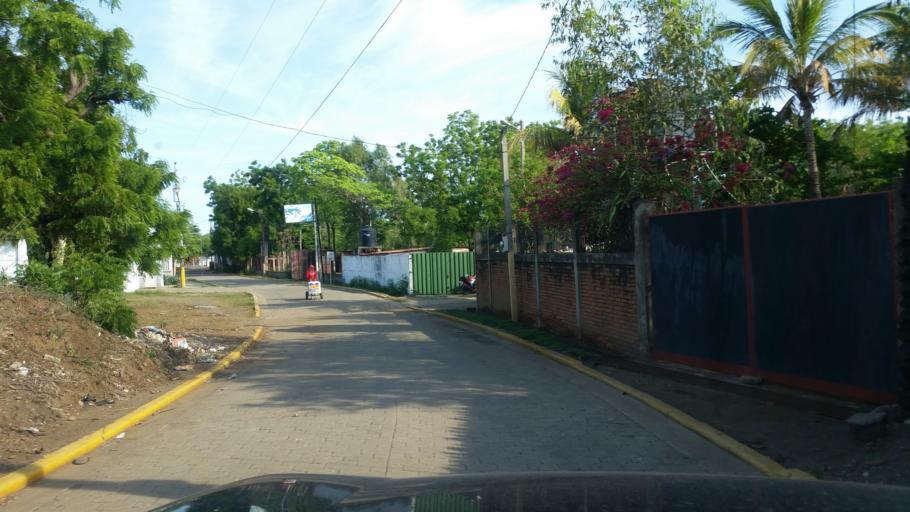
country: NI
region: Managua
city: Masachapa
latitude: 11.7791
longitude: -86.5168
